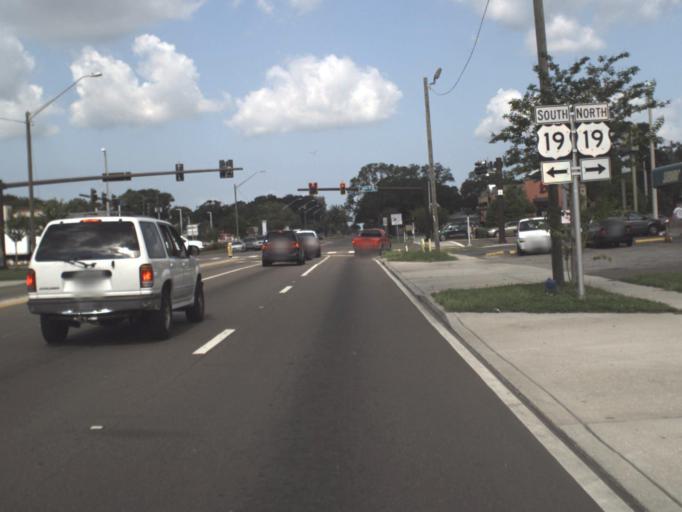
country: US
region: Florida
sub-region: Pinellas County
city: Saint Petersburg
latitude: 27.7774
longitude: -82.6785
